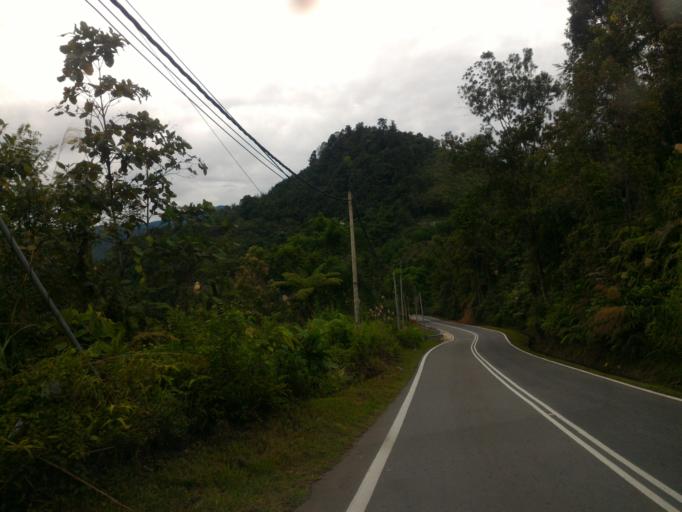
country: MY
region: Sabah
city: Donggongon
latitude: 5.8771
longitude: 116.2401
